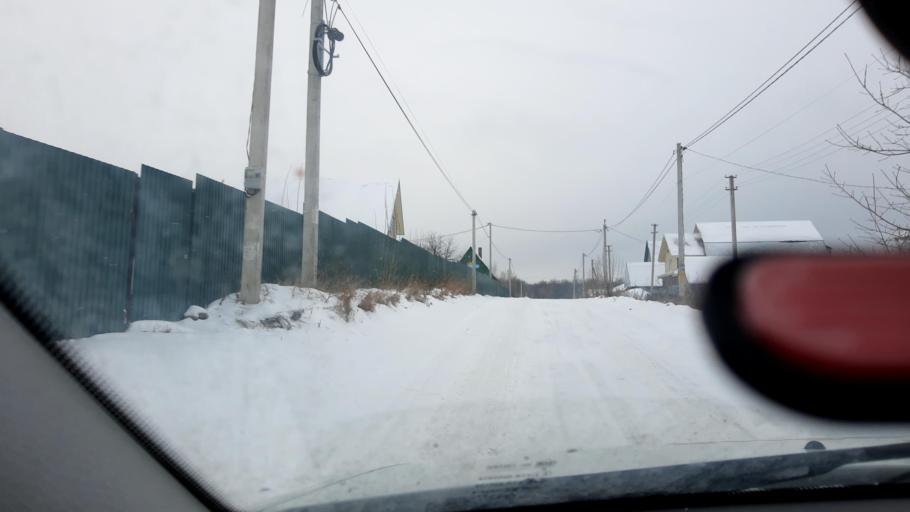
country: RU
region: Bashkortostan
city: Kabakovo
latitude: 54.6305
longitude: 56.0816
